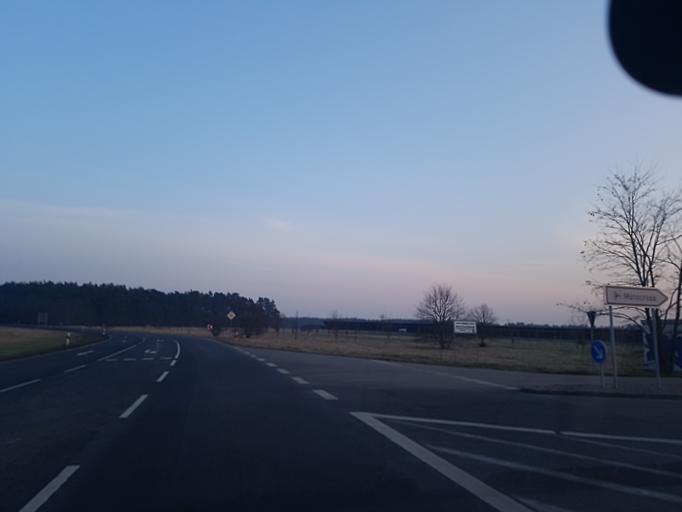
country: DE
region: Saxony-Anhalt
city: Jessen
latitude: 51.8046
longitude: 12.9223
